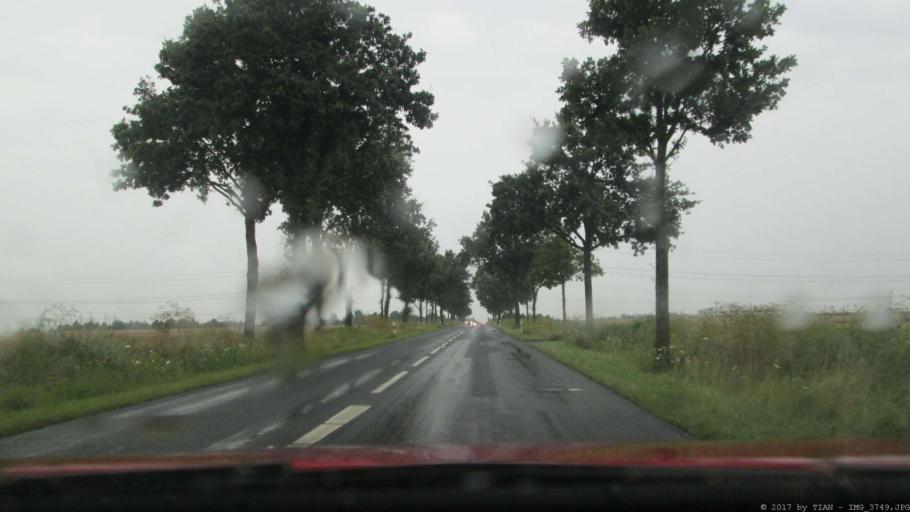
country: DE
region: Lower Saxony
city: Wolfsburg
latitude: 52.3658
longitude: 10.7472
